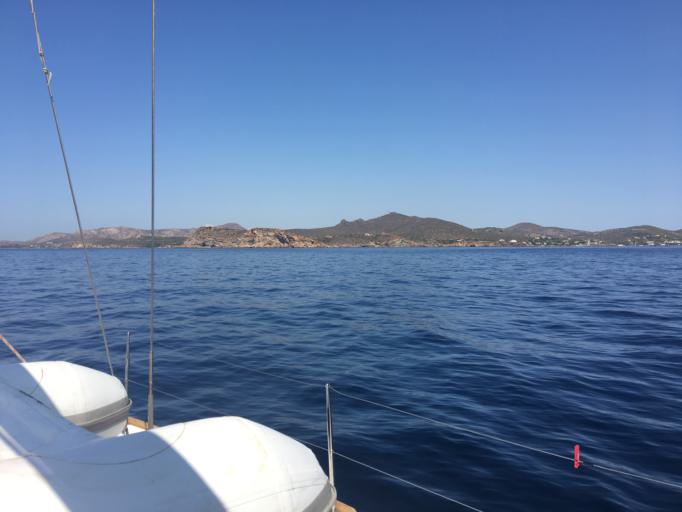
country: GR
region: Attica
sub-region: Nomarchia Anatolikis Attikis
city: Lavrio
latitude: 37.6367
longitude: 24.0401
